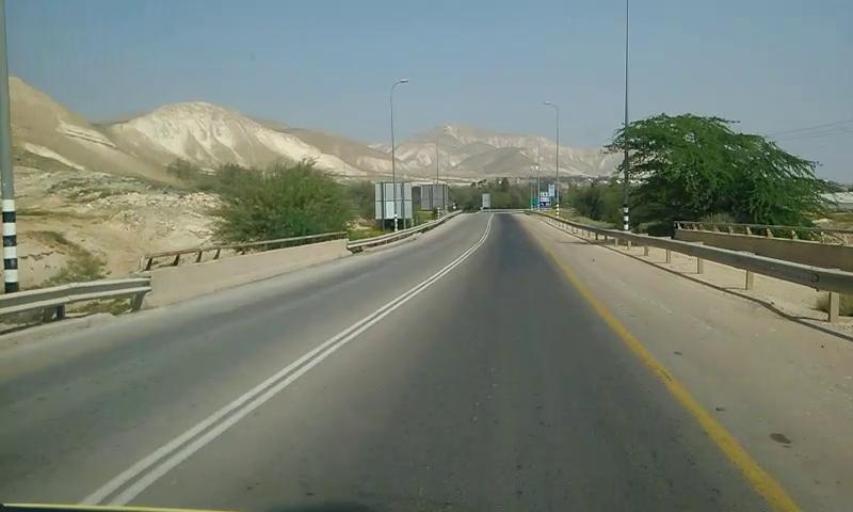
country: PS
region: West Bank
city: Al Fasayil
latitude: 32.0506
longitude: 35.4648
